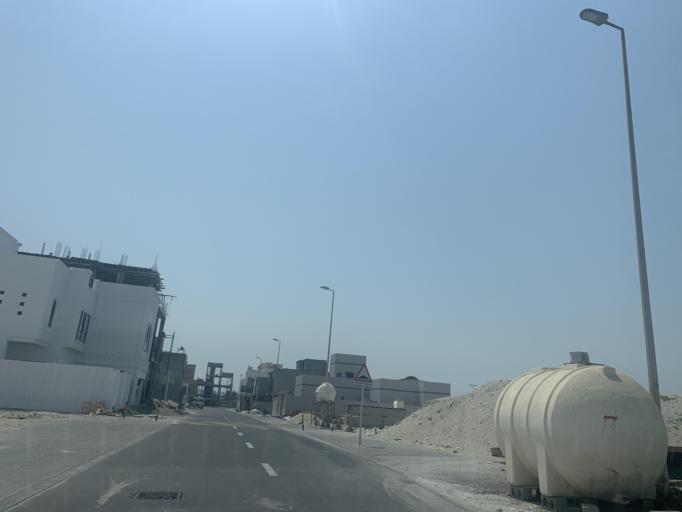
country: BH
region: Muharraq
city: Al Hadd
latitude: 26.2415
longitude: 50.6612
